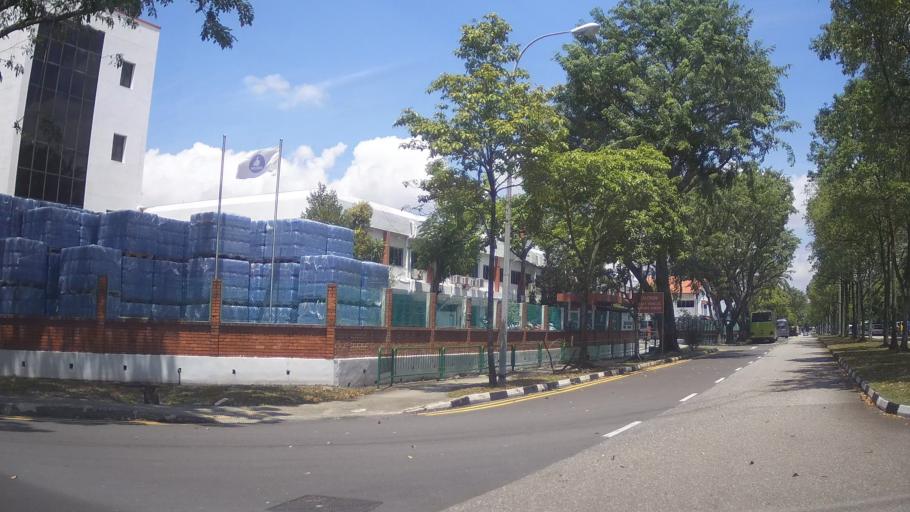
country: SG
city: Singapore
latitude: 1.3312
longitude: 103.7185
